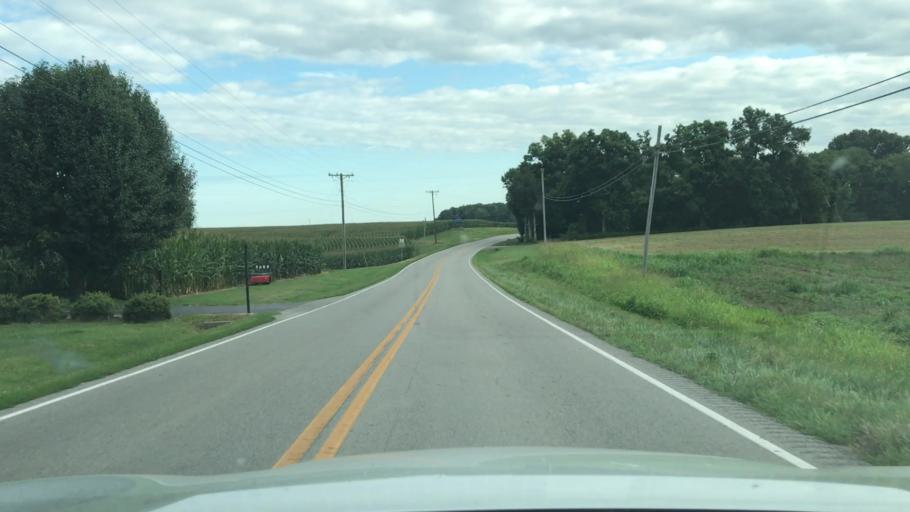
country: US
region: Kentucky
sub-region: Todd County
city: Elkton
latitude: 36.7885
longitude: -87.1641
